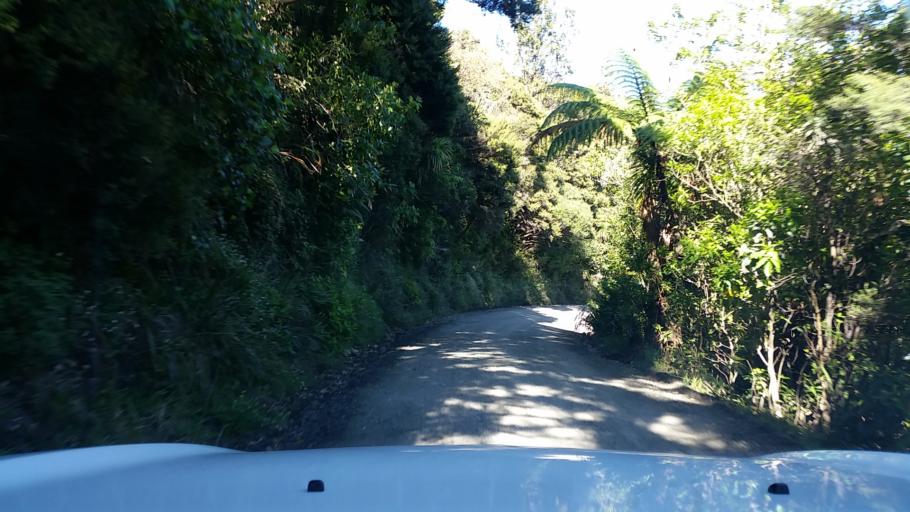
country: NZ
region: Auckland
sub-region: Auckland
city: Titirangi
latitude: -37.0281
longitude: 174.5282
